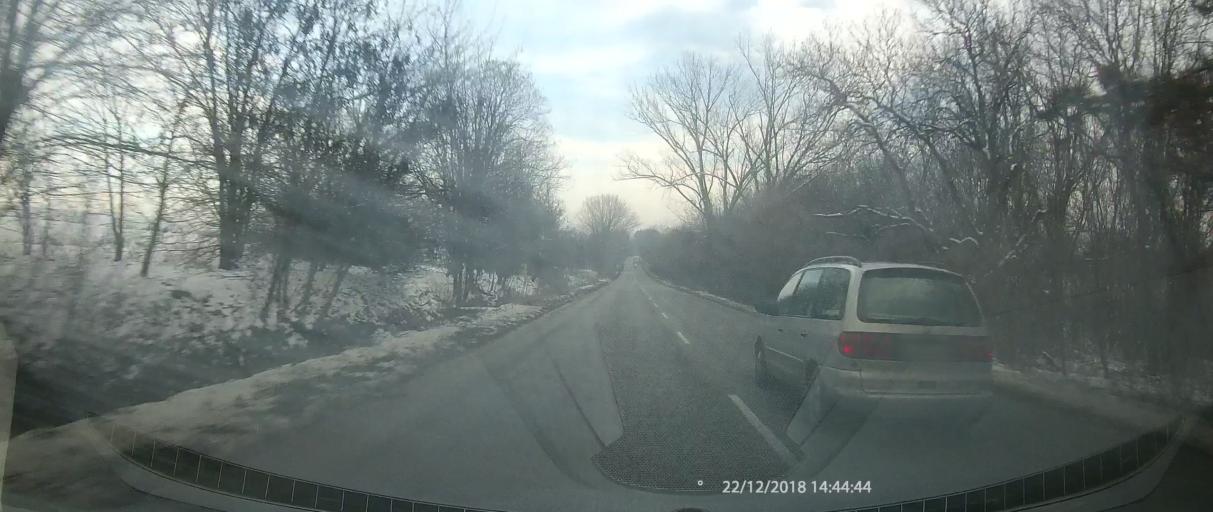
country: BG
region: Veliko Turnovo
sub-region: Obshtina Pavlikeni
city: Pavlikeni
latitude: 43.4169
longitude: 25.3171
